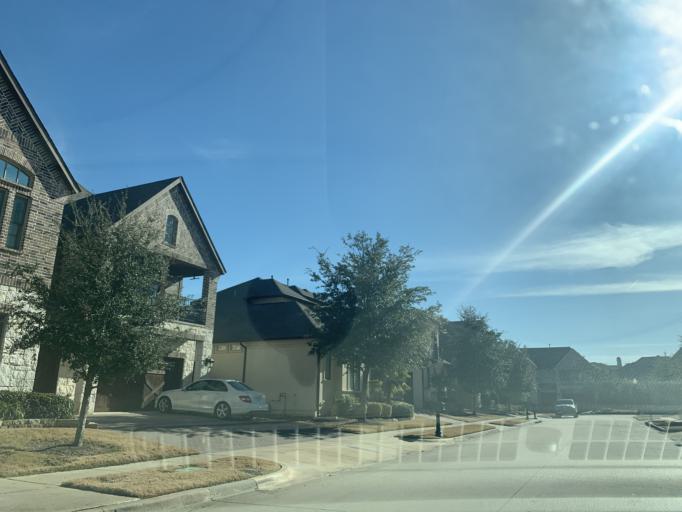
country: US
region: Texas
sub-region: Denton County
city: The Colony
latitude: 33.0597
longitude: -96.8180
